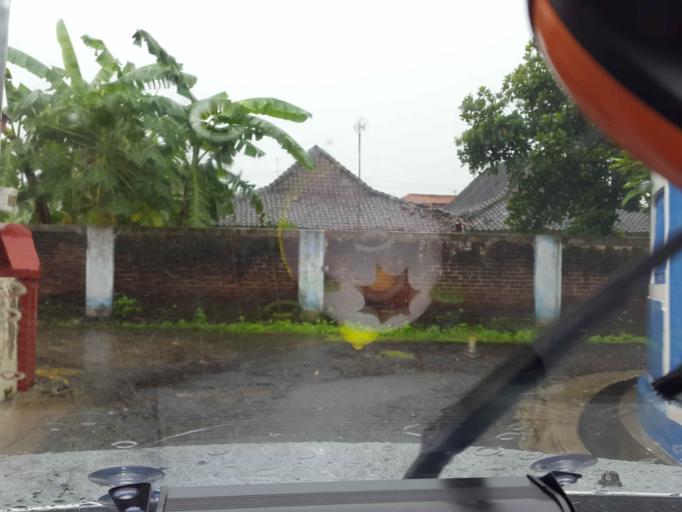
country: ID
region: Central Java
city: Jaten
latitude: -7.6042
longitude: 110.9772
